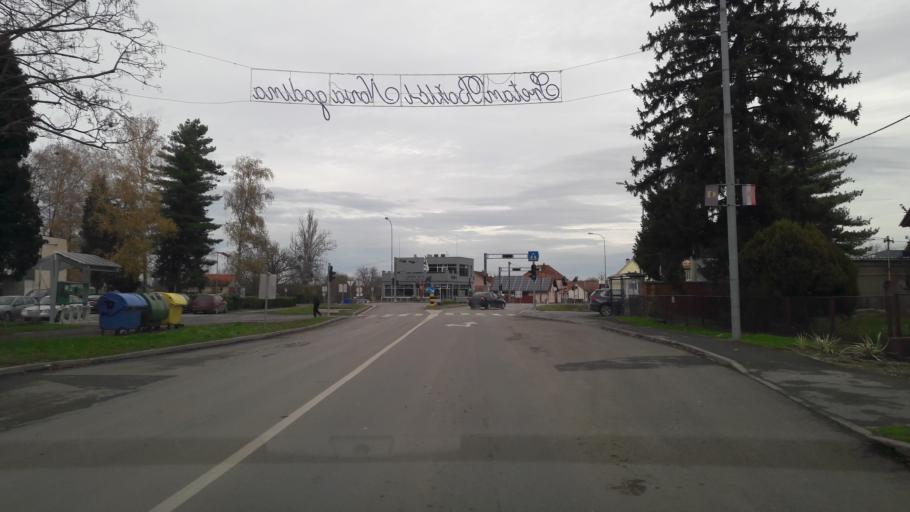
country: HR
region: Virovitick-Podravska
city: Orahovica
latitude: 45.5477
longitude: 17.9018
